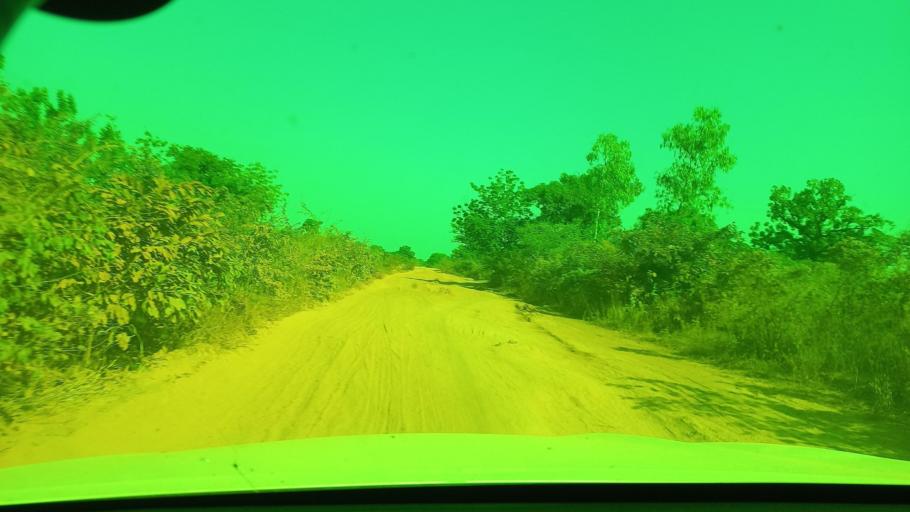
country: ML
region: Bamako
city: Bamako
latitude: 12.3966
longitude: -7.9830
